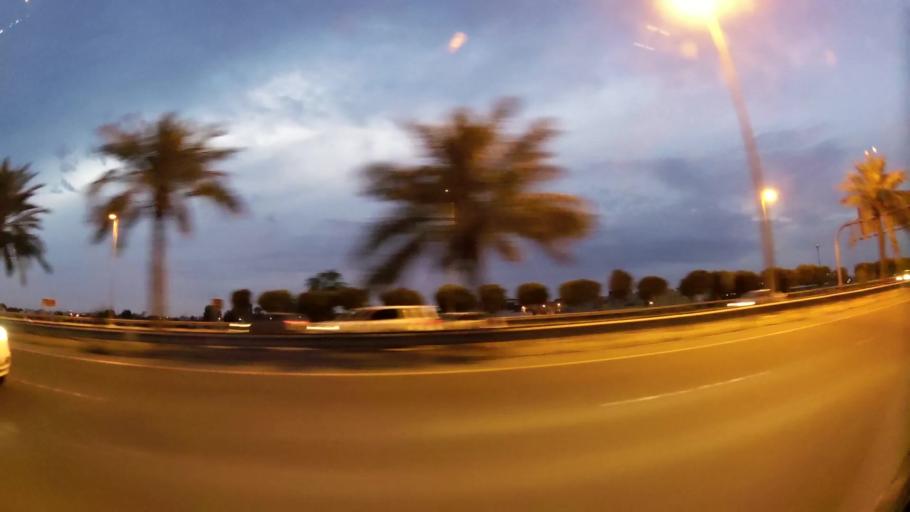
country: BH
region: Northern
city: Madinat `Isa
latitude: 26.1947
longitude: 50.5068
